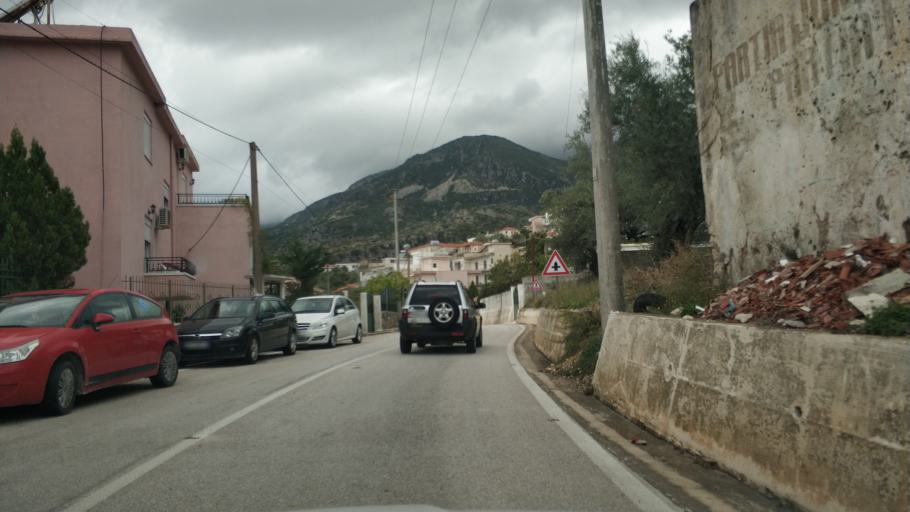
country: AL
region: Vlore
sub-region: Rrethi i Vlores
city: Vranisht
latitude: 40.1490
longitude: 19.6423
